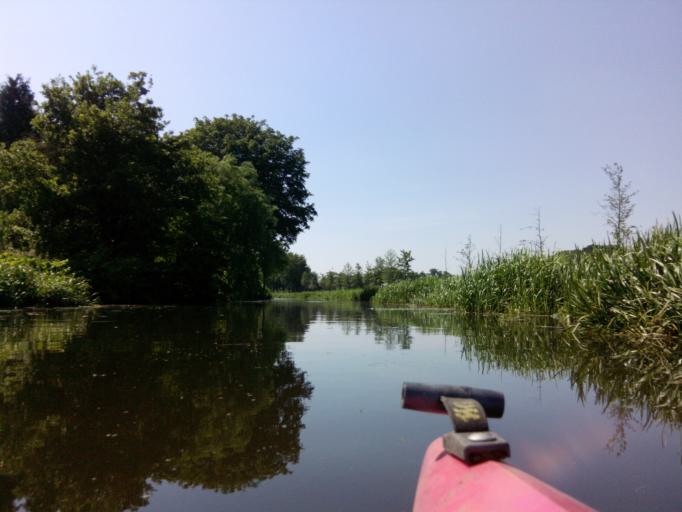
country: NL
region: Utrecht
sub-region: Gemeente Amersfoort
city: Randenbroek
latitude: 52.1180
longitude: 5.4006
